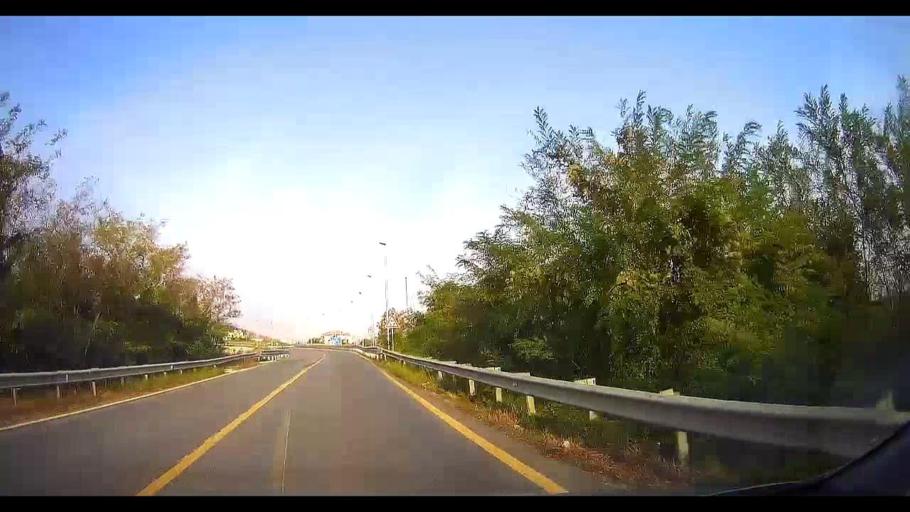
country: IT
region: Calabria
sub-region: Provincia di Cosenza
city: Cariati
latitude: 39.5227
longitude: 16.8984
